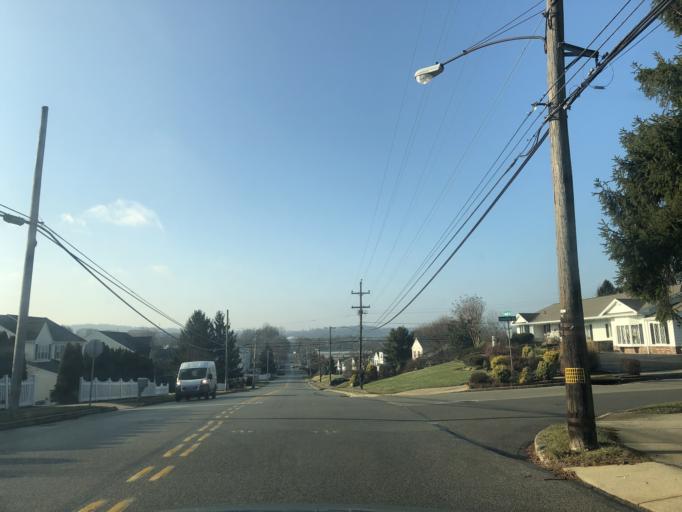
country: US
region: Pennsylvania
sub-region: Montgomery County
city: Conshohocken
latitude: 40.0887
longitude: -75.3039
